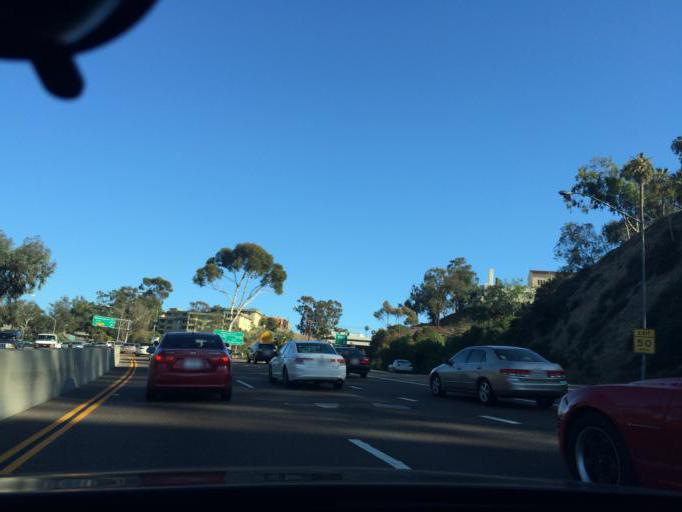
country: US
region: California
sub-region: San Diego County
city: San Diego
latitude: 32.7541
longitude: -117.1584
